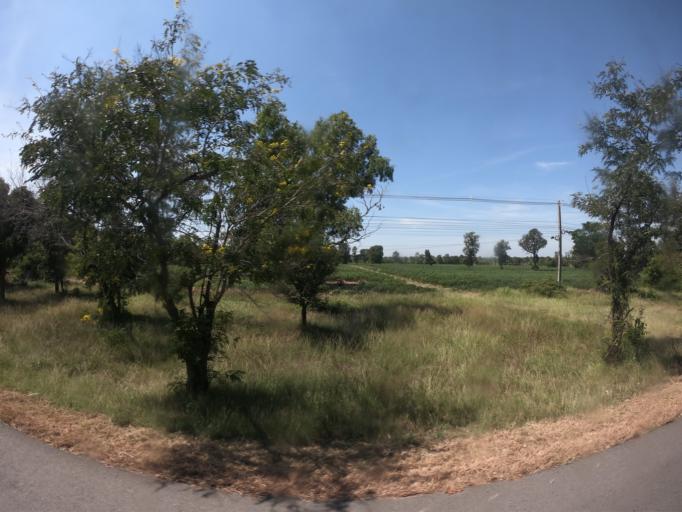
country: TH
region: Khon Kaen
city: Phon
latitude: 15.7742
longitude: 102.6066
